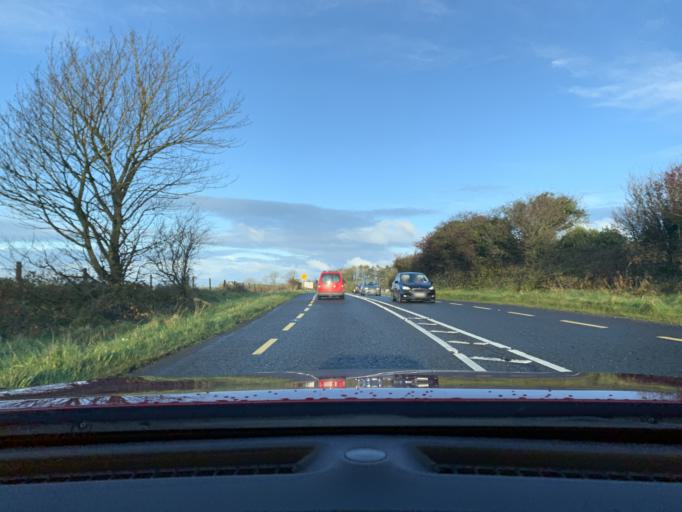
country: IE
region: Connaught
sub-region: Sligo
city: Sligo
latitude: 54.3609
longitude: -8.5241
